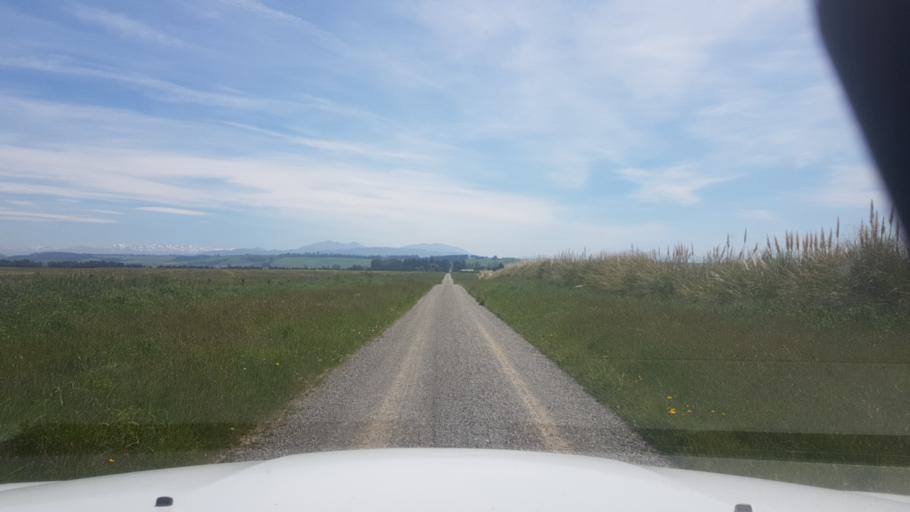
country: NZ
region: Canterbury
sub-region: Timaru District
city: Pleasant Point
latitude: -44.2336
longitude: 171.1676
